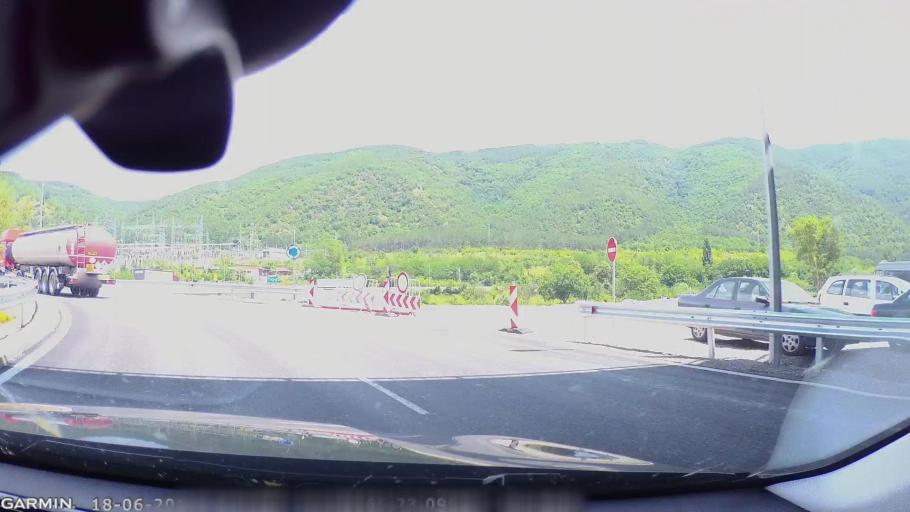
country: BG
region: Blagoevgrad
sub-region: Obshtina Blagoevgrad
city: Blagoevgrad
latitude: 41.9615
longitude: 23.0988
